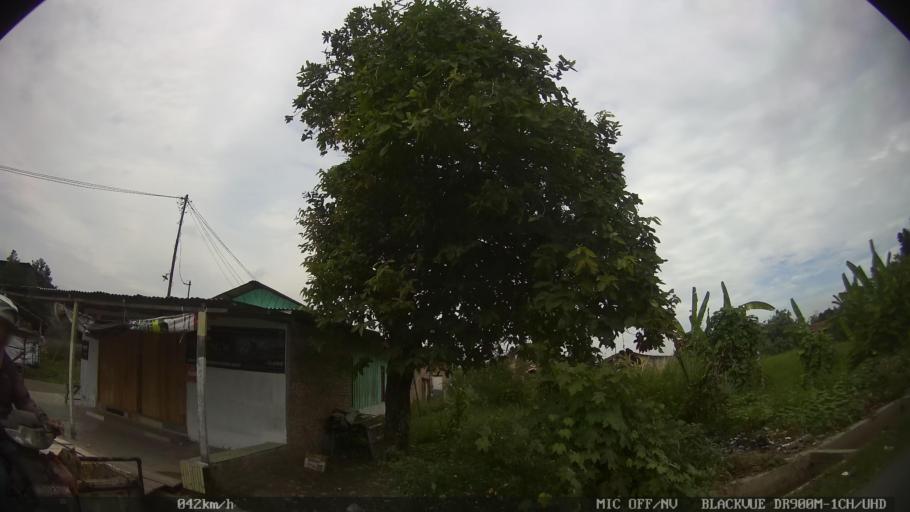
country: ID
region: North Sumatra
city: Sunggal
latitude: 3.6151
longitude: 98.6004
